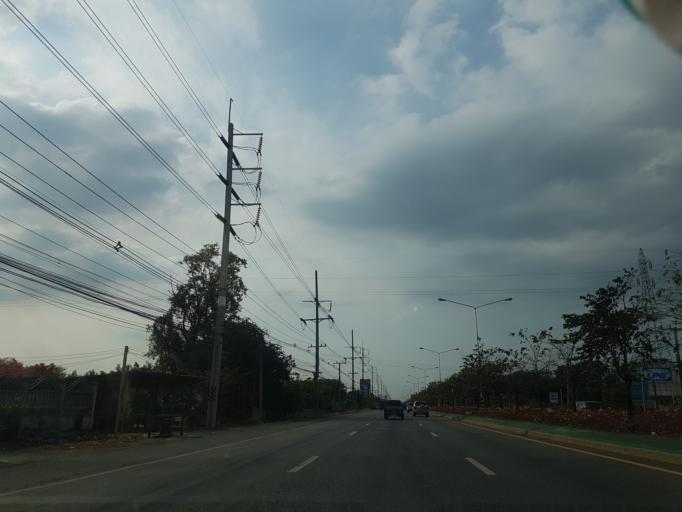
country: TH
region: Sara Buri
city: Phra Phutthabat
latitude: 14.7392
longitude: 100.7683
